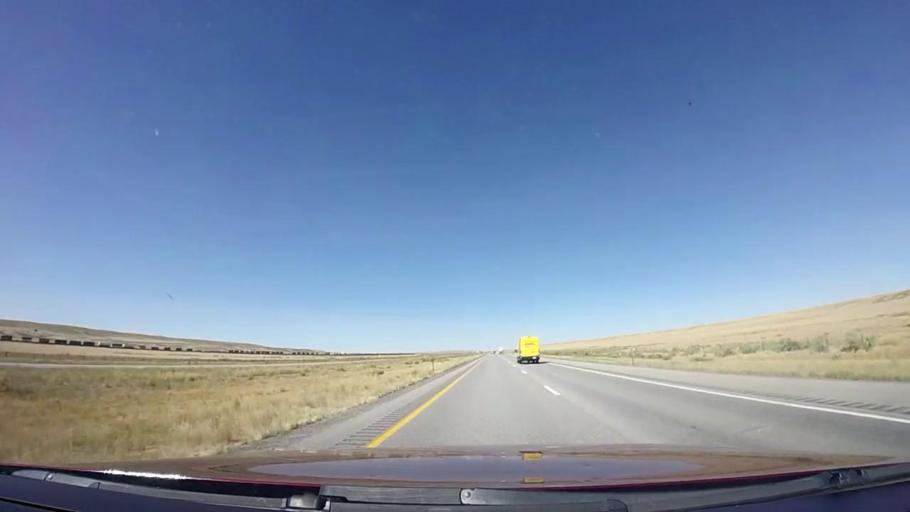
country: US
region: Wyoming
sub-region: Carbon County
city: Rawlins
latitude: 41.6588
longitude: -108.0828
